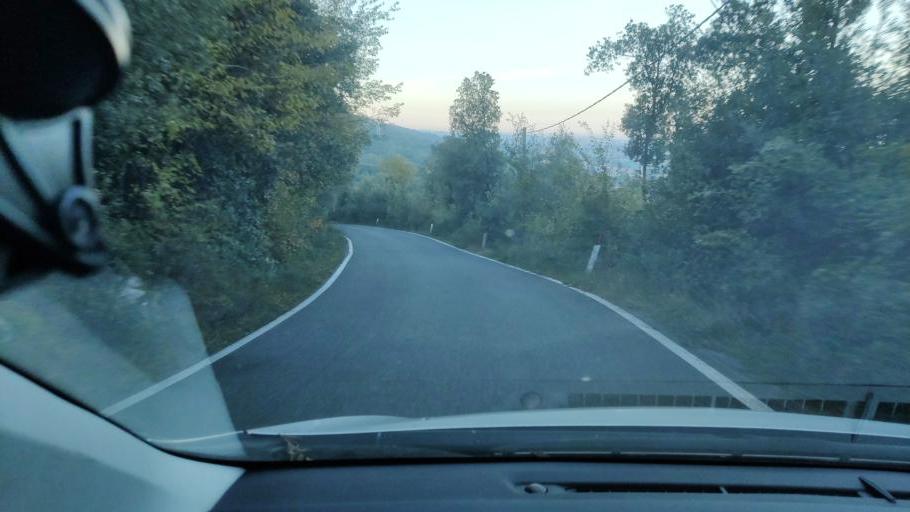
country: IT
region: Umbria
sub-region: Provincia di Terni
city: Amelia
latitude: 42.5845
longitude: 12.4325
